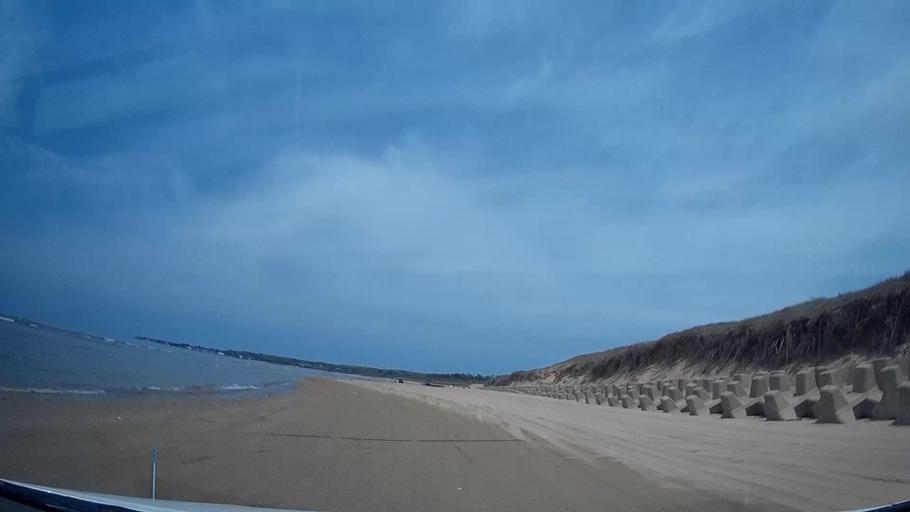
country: JP
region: Ishikawa
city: Hakui
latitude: 36.8997
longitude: 136.7671
